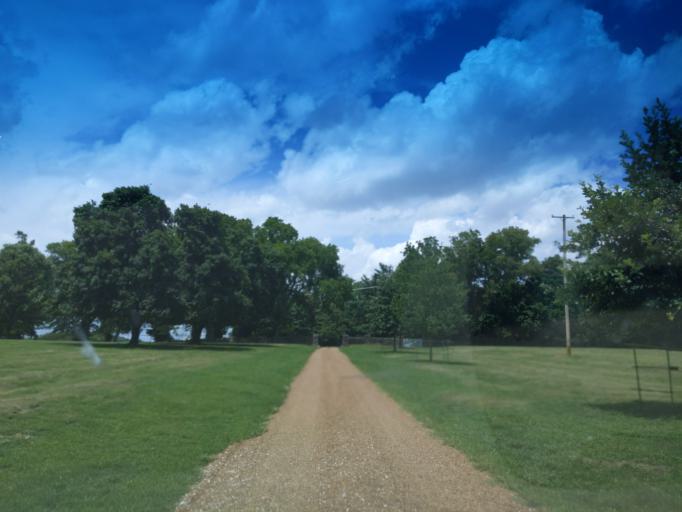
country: US
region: Tennessee
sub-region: Williamson County
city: Brentwood Estates
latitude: 36.0171
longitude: -86.7708
